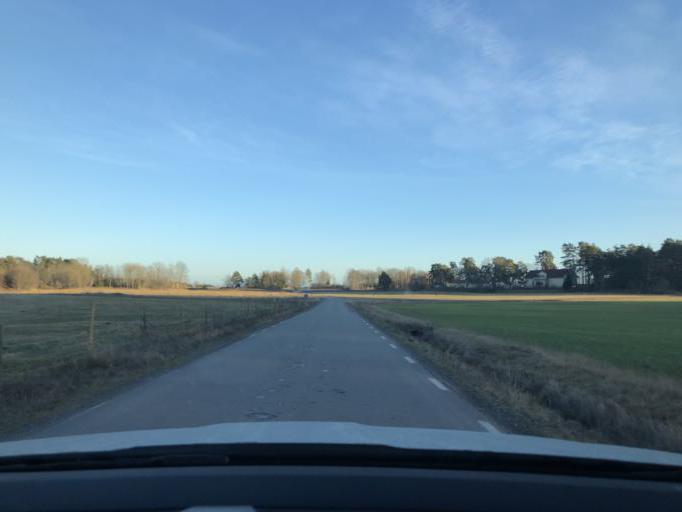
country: SE
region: Soedermanland
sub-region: Eskilstuna Kommun
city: Arla
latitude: 59.4137
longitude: 16.6901
